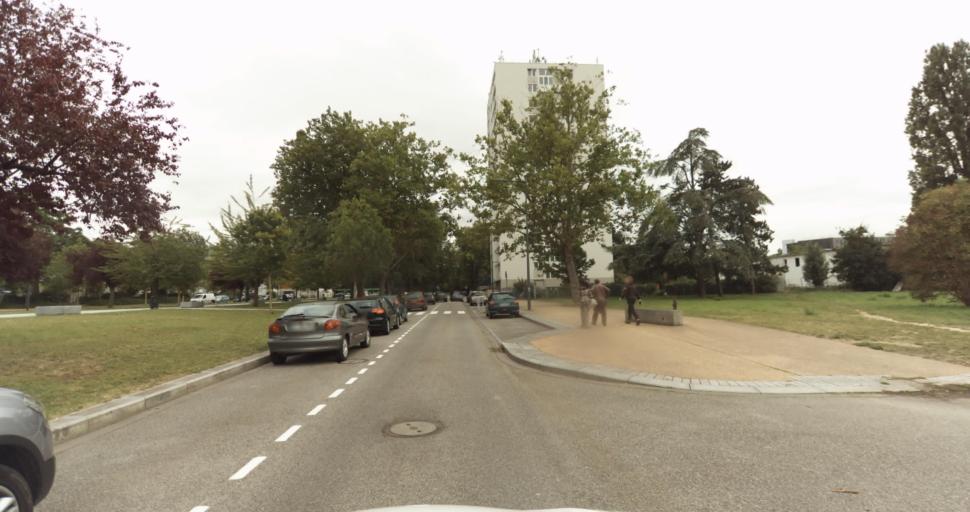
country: FR
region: Haute-Normandie
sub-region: Departement de l'Eure
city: Evreux
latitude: 49.0067
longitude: 1.1569
